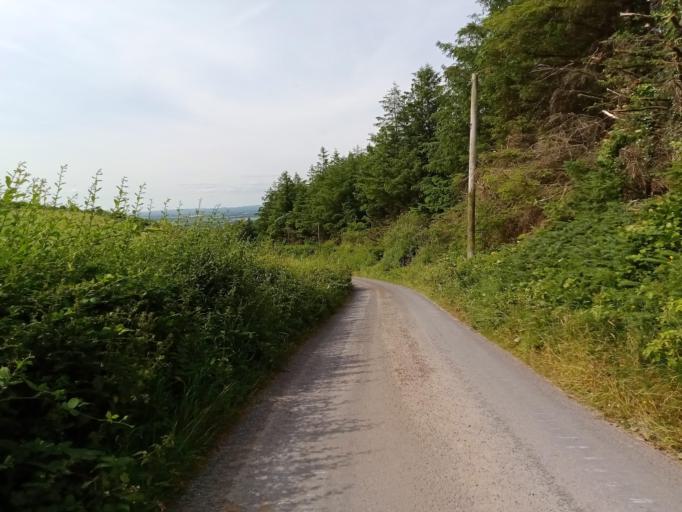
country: IE
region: Leinster
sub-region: Laois
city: Rathdowney
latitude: 52.7995
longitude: -7.4652
